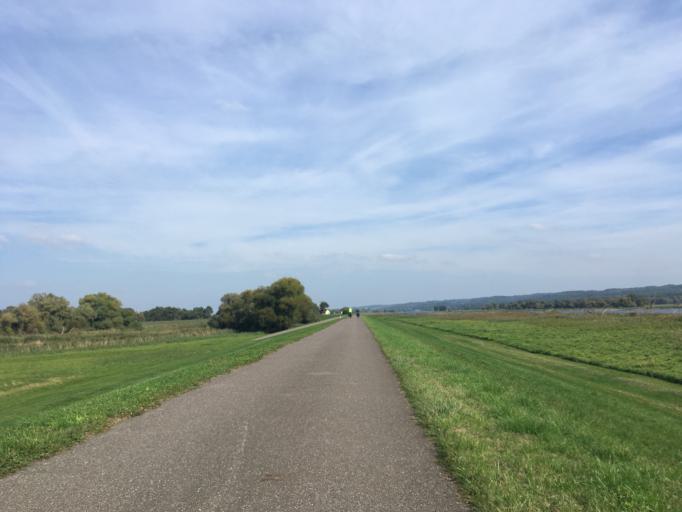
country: DE
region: Brandenburg
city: Schoneberg
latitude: 52.9804
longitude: 14.1833
